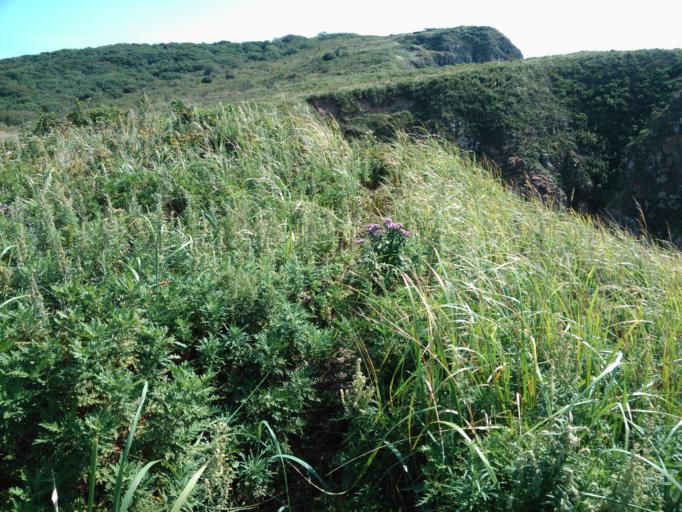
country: RU
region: Primorskiy
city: Russkiy
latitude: 42.9337
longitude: 131.8258
